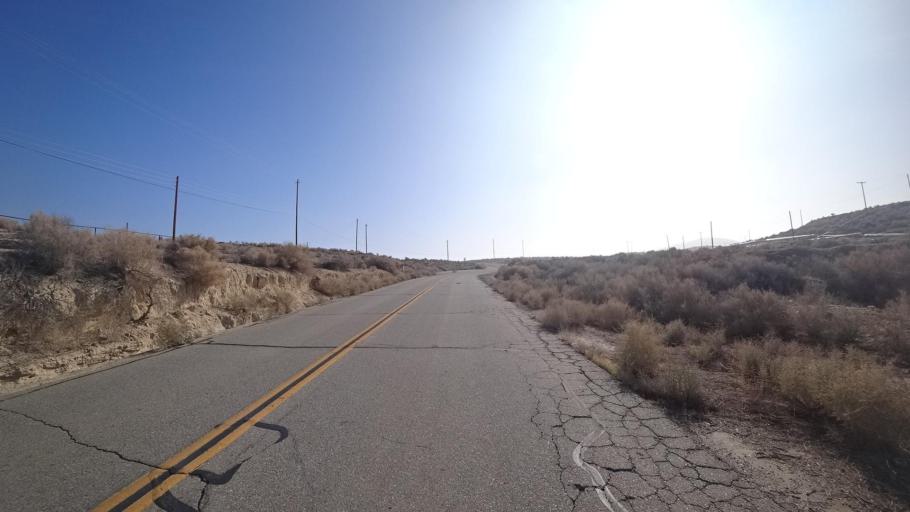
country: US
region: California
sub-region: Kern County
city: Taft Heights
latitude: 35.1495
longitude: -119.5156
